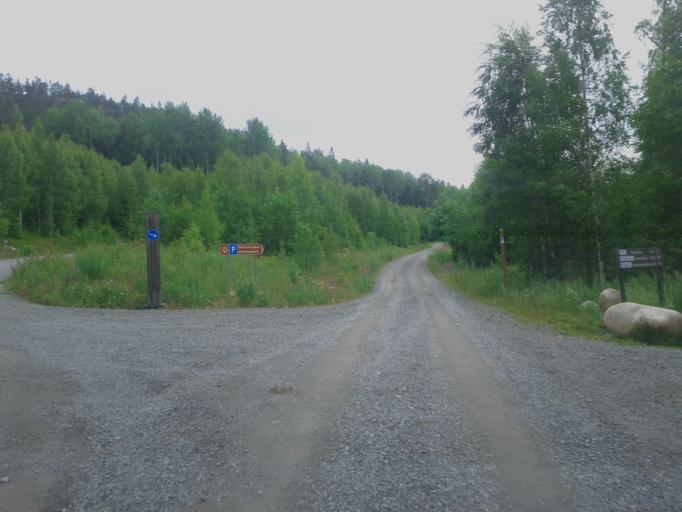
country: SE
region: Vaesternorrland
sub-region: OErnskoeldsviks Kommun
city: Bjasta
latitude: 63.0837
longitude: 18.4790
